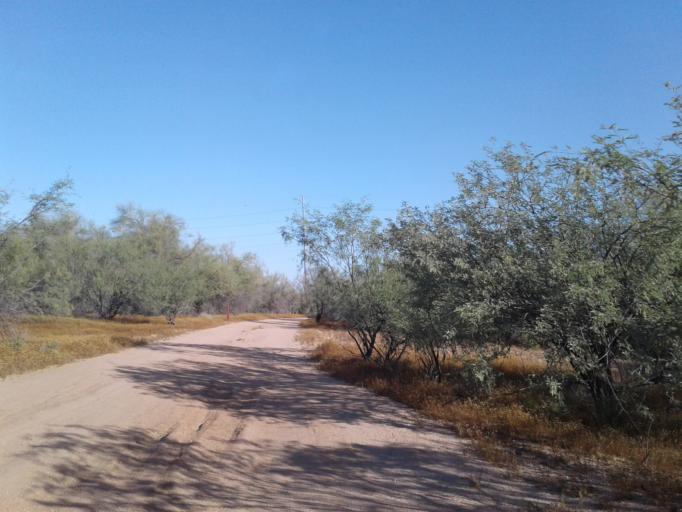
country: US
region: Arizona
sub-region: Maricopa County
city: Paradise Valley
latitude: 33.6682
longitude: -112.0050
